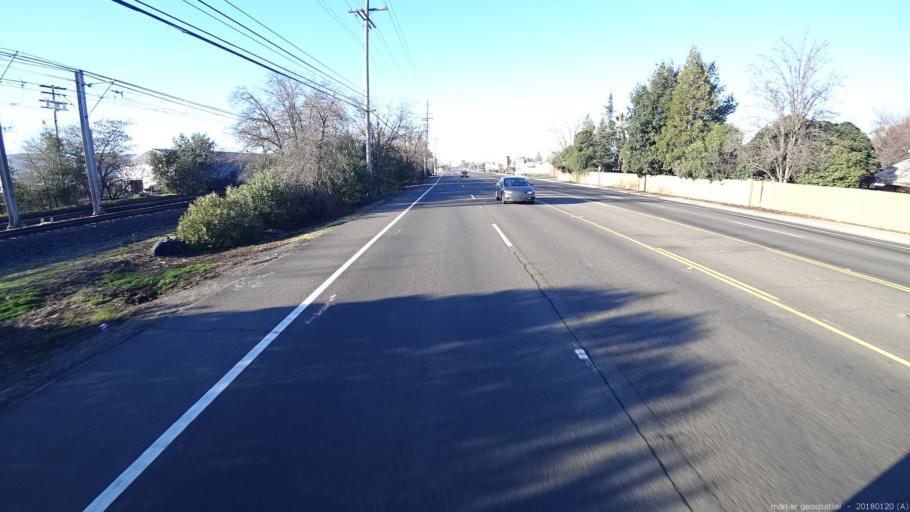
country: US
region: California
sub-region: Sacramento County
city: La Riviera
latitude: 38.5737
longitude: -121.3339
